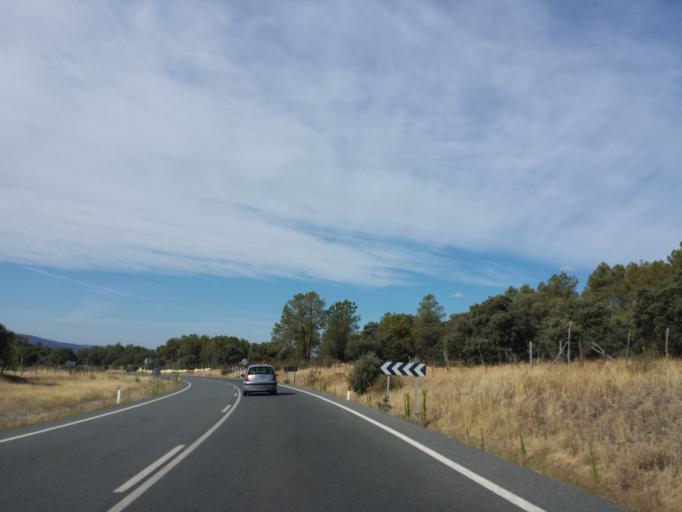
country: ES
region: Castille and Leon
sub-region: Provincia de Avila
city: Casavieja
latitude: 40.2855
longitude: -4.7298
